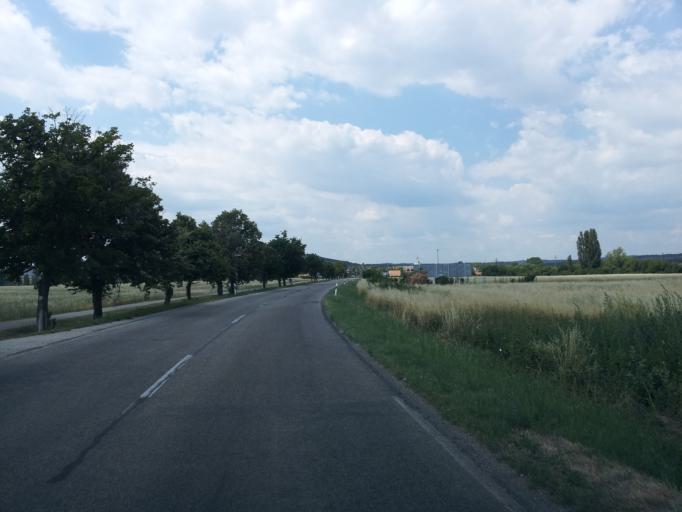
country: HU
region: Veszprem
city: Tihany
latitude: 46.9231
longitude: 17.8442
